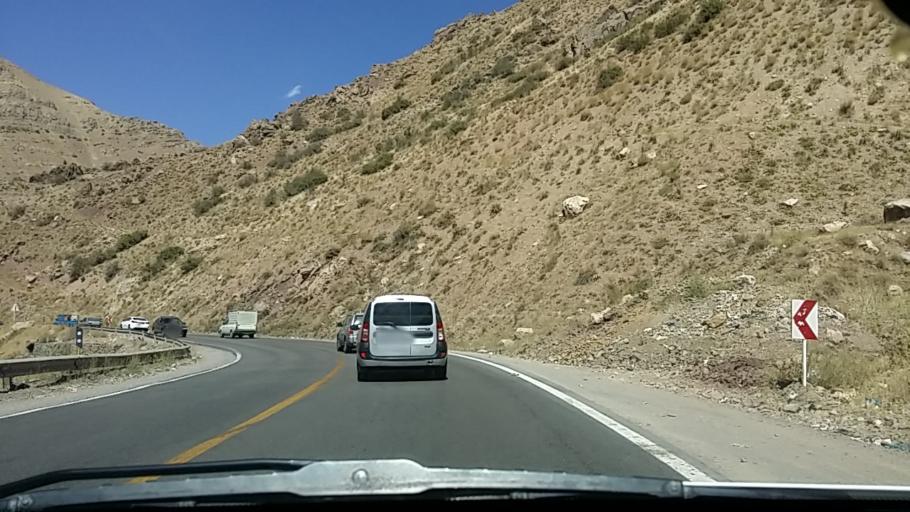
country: IR
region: Tehran
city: Tajrish
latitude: 36.0686
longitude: 51.3107
